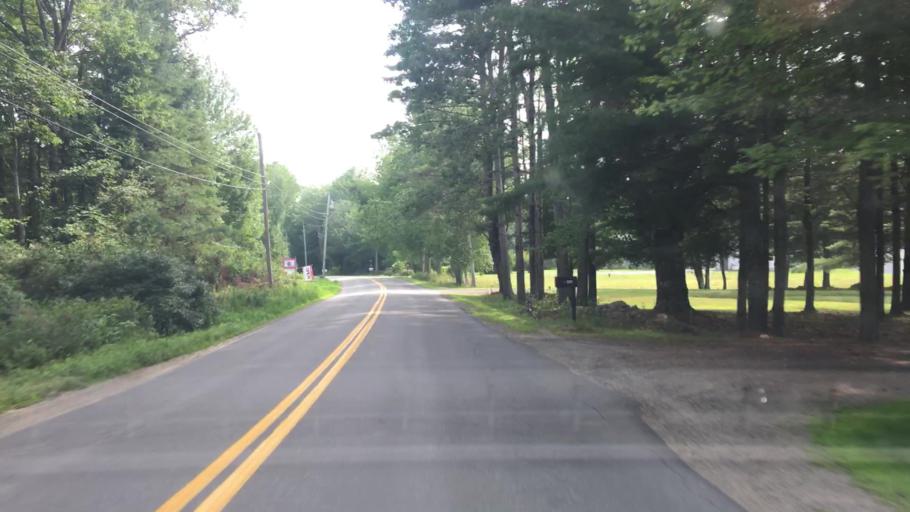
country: US
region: Maine
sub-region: Lincoln County
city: Jefferson
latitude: 44.1758
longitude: -69.4650
